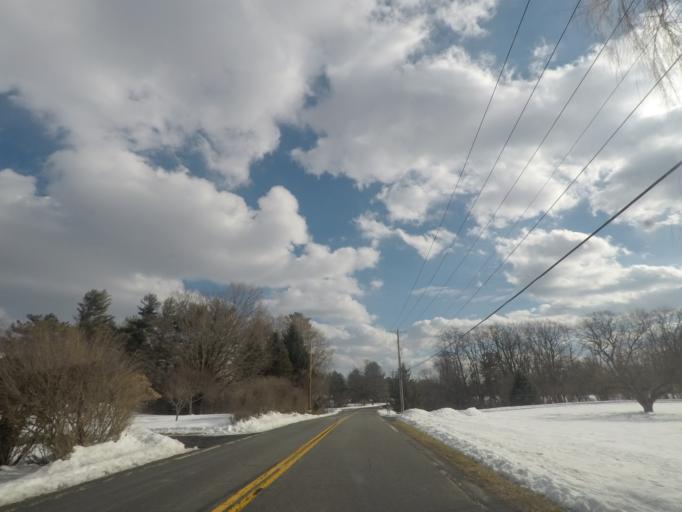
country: US
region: New York
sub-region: Schenectady County
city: Niskayuna
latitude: 42.8330
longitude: -73.8659
